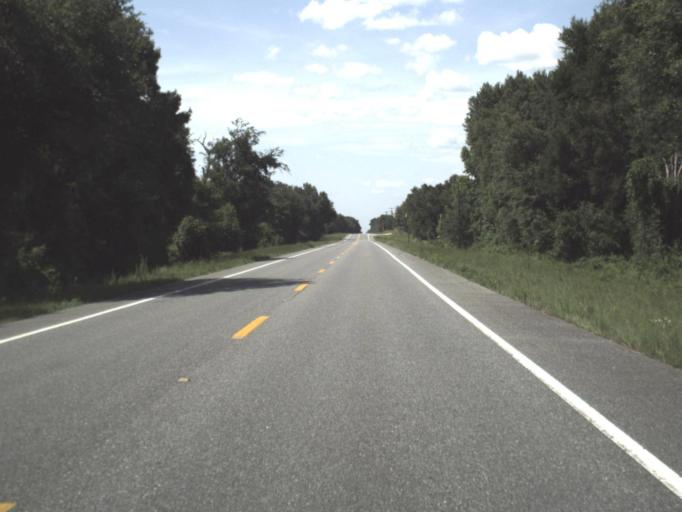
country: US
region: Florida
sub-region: Alachua County
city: High Springs
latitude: 29.7746
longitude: -82.7407
